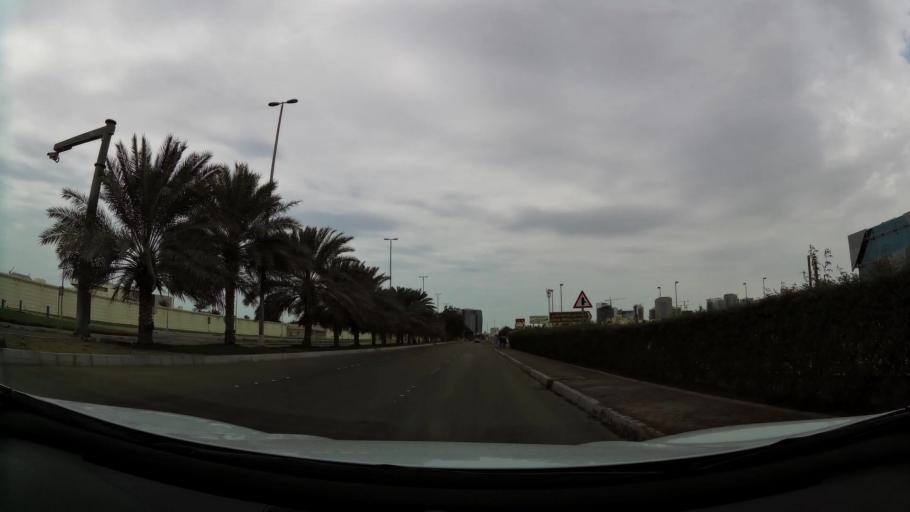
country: AE
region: Abu Dhabi
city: Abu Dhabi
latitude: 24.4204
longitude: 54.4275
